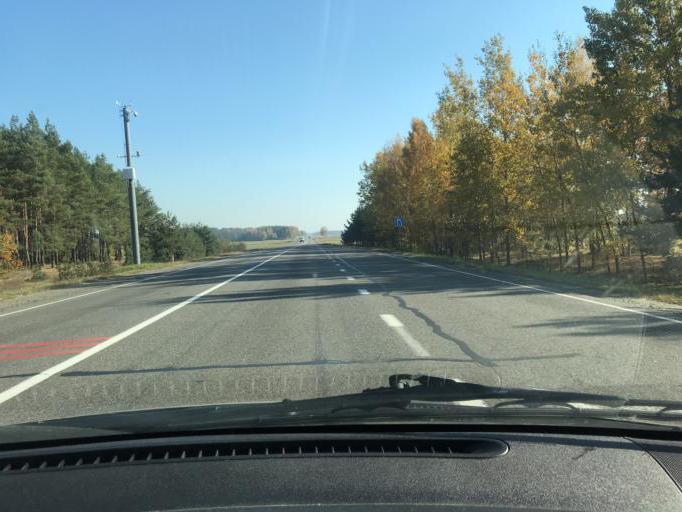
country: BY
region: Brest
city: Davyd-Haradok
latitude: 52.2446
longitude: 27.1431
